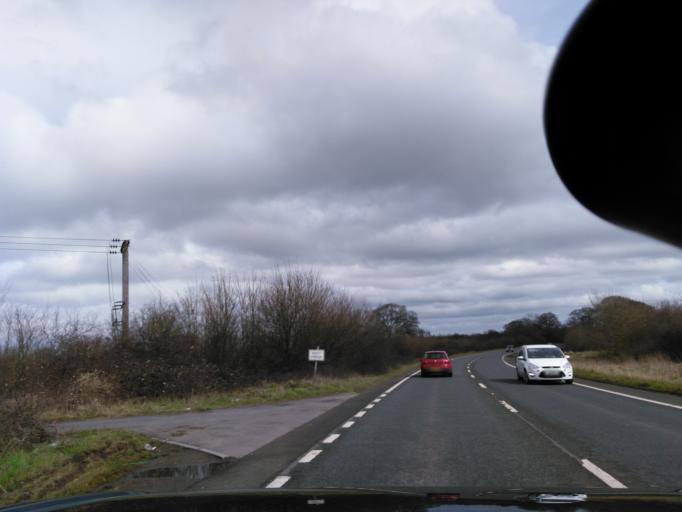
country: GB
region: England
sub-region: Wiltshire
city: Melksham
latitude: 51.3350
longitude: -2.1485
